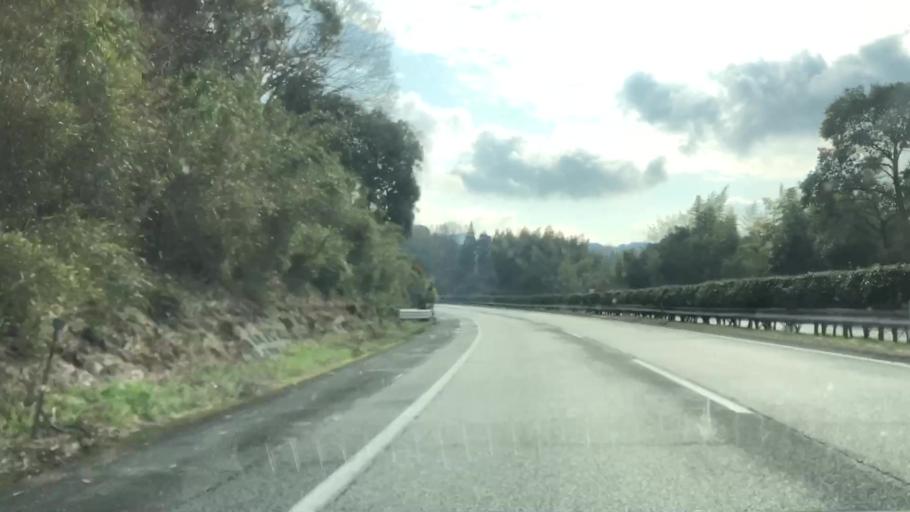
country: JP
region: Kumamoto
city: Tamana
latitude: 33.0083
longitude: 130.5829
